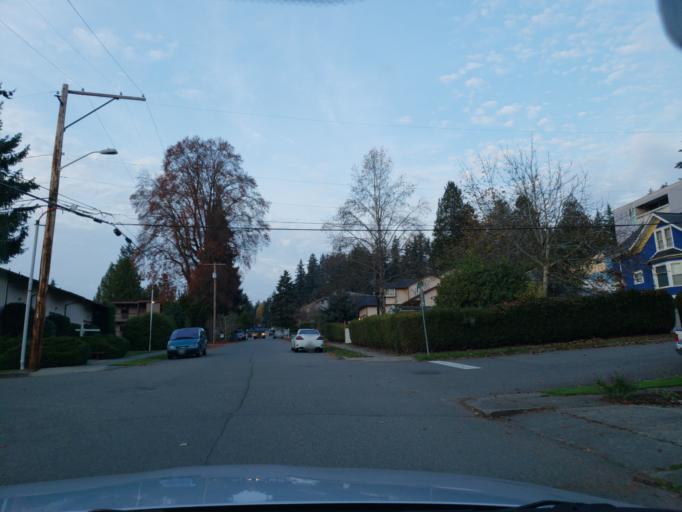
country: US
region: Washington
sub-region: King County
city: Bothell
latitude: 47.7637
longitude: -122.2033
